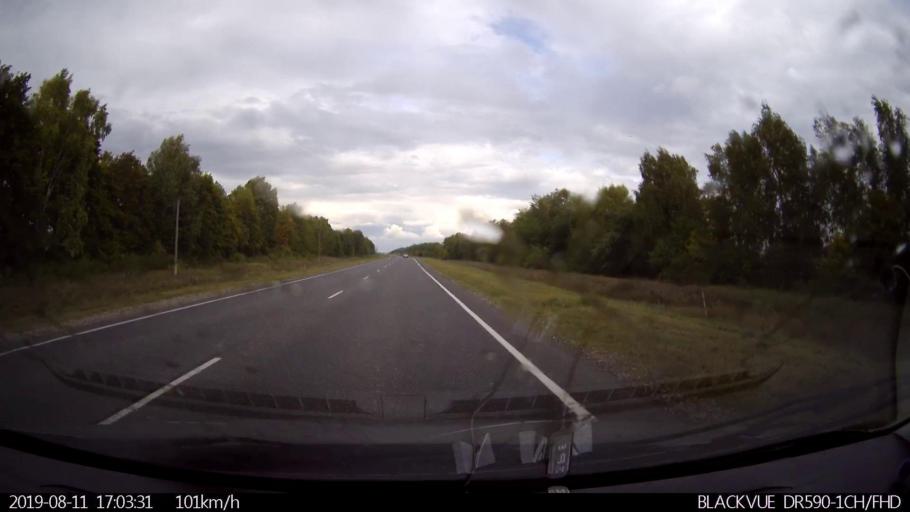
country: RU
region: Ulyanovsk
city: Mayna
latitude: 54.3027
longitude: 47.7421
